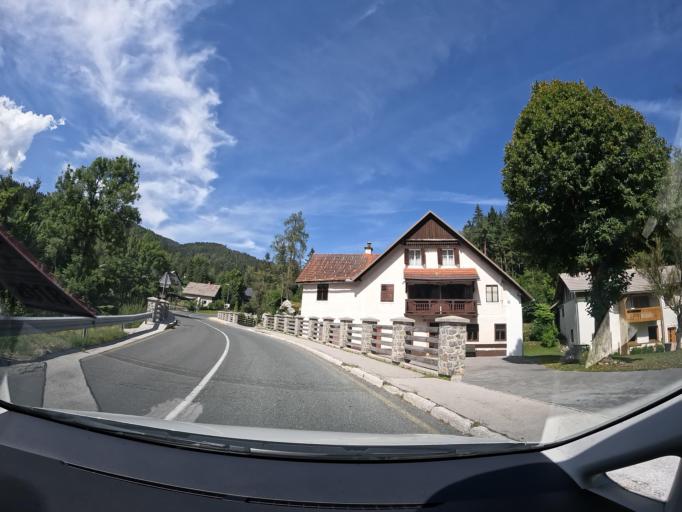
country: AT
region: Carinthia
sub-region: Politischer Bezirk Klagenfurt Land
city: Moosburg
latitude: 46.6578
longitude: 14.1402
